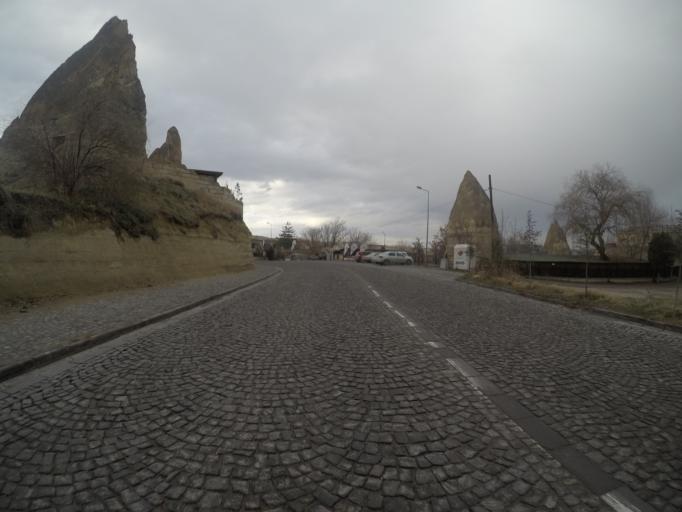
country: TR
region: Nevsehir
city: Goereme
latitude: 38.6441
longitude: 34.8344
